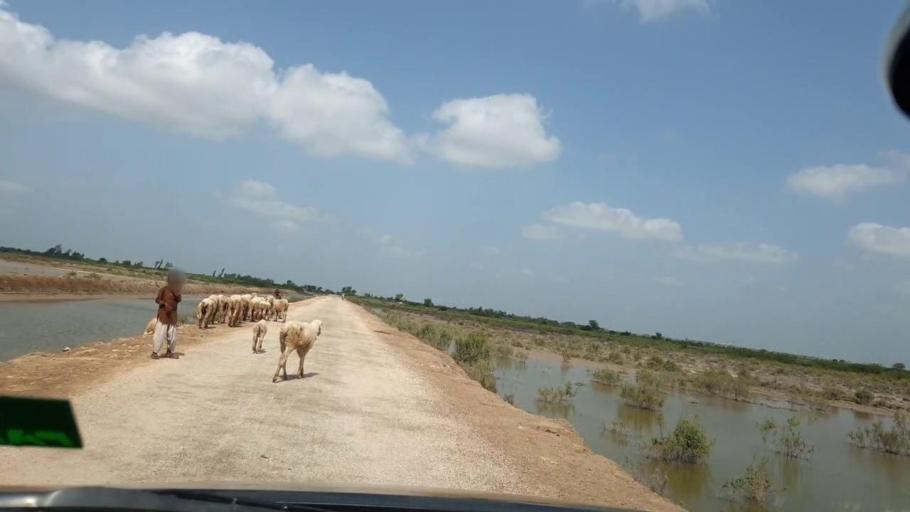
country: PK
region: Sindh
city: Kadhan
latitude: 24.5979
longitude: 69.1274
